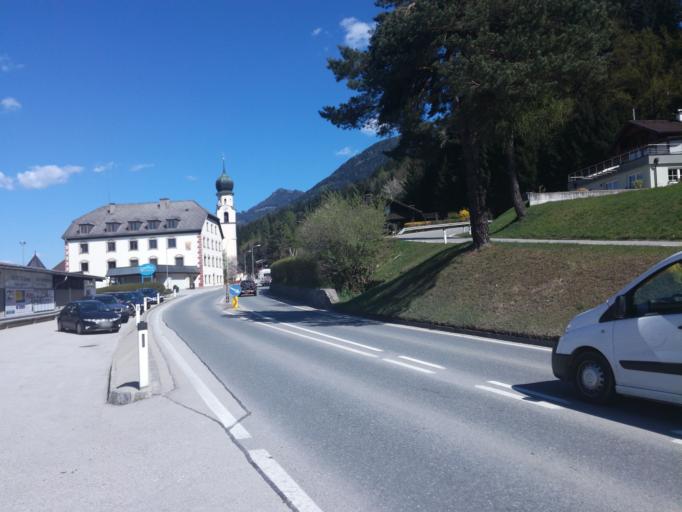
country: AT
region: Tyrol
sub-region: Politischer Bezirk Schwaz
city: Pill
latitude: 47.3194
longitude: 11.6797
